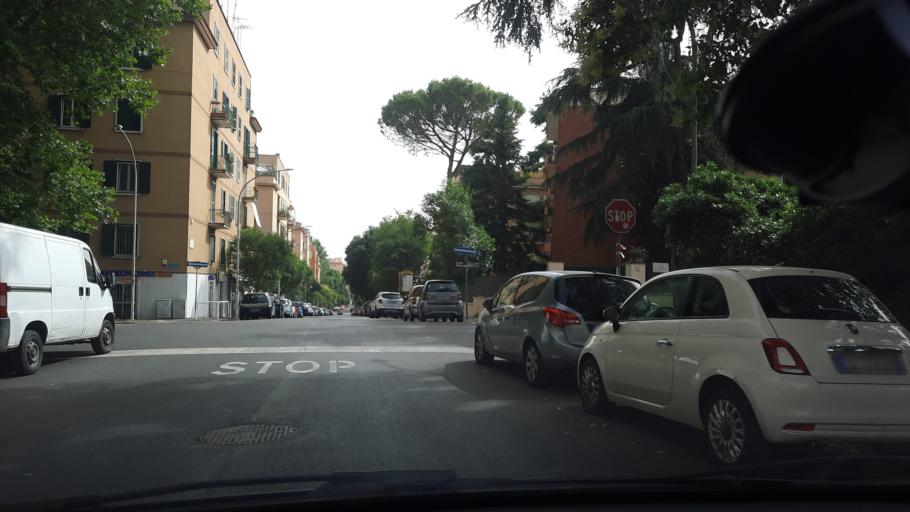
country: IT
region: Latium
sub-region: Citta metropolitana di Roma Capitale
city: Rome
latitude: 41.8586
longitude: 12.4897
